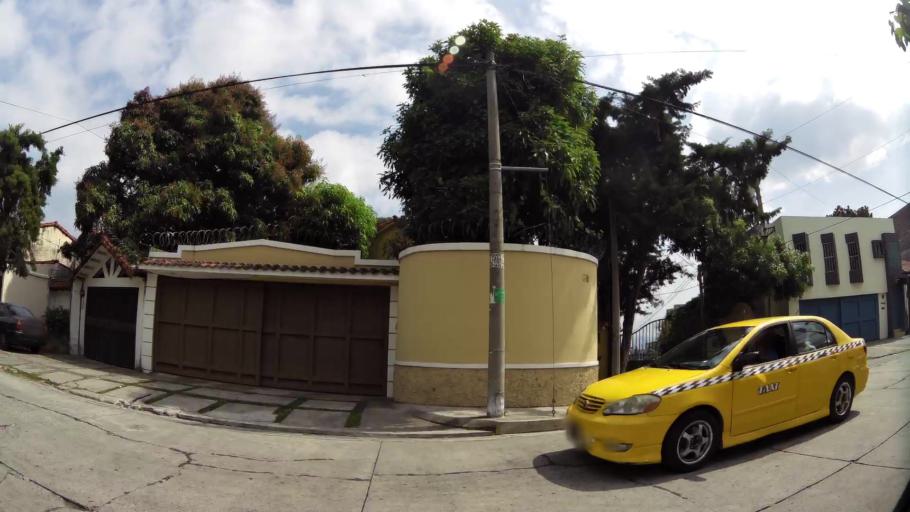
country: SV
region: San Salvador
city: Mejicanos
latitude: 13.7118
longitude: -89.2436
